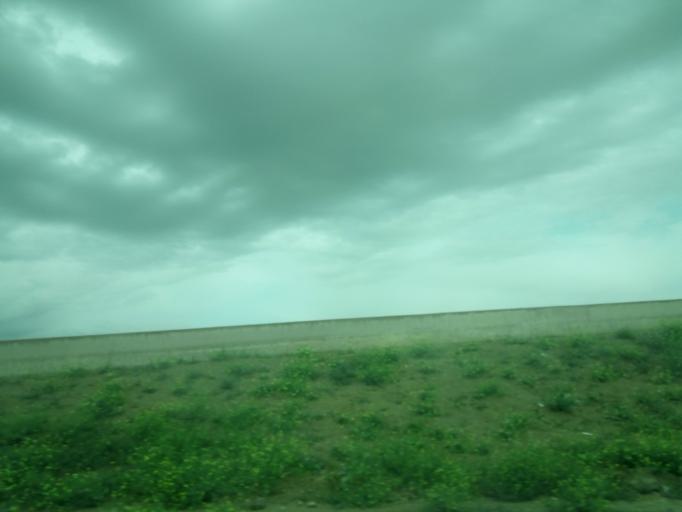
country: DZ
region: Medea
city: Ksar el Boukhari
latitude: 35.8843
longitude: 2.7355
